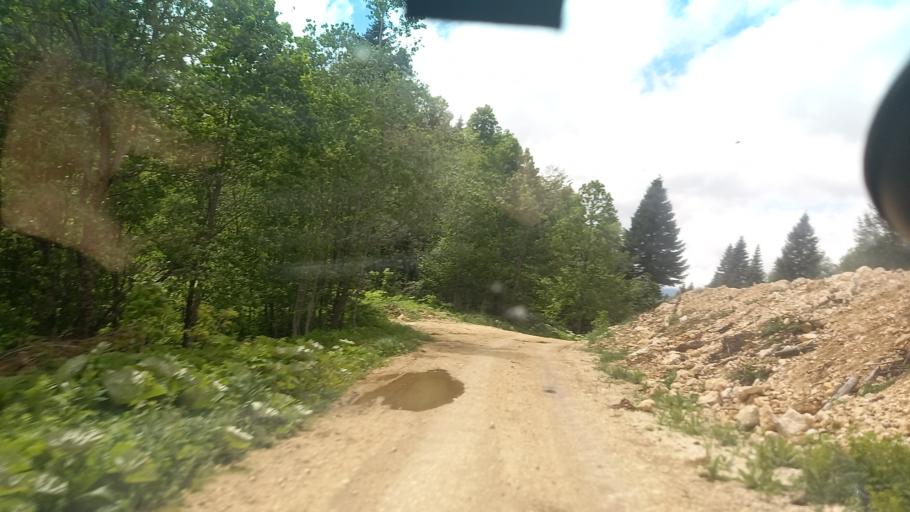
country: RU
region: Krasnodarskiy
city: Neftegorsk
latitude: 44.0552
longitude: 39.8185
